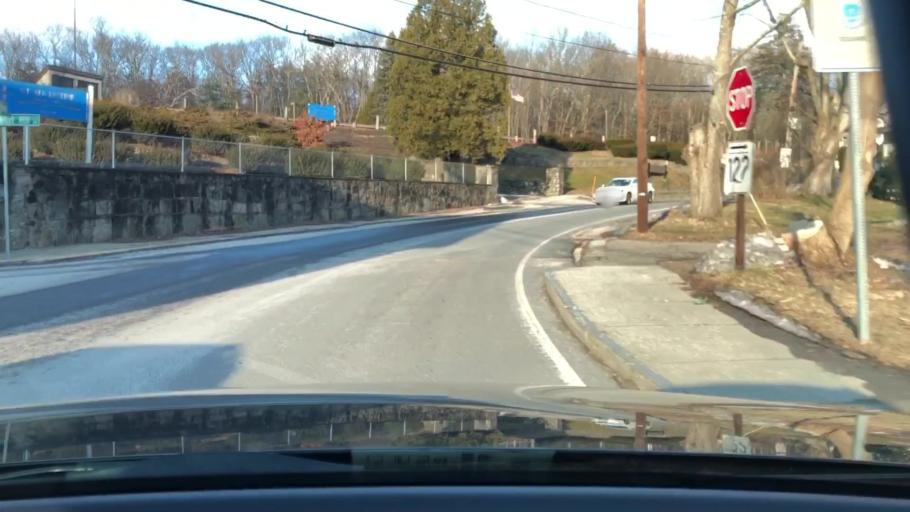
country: US
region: Massachusetts
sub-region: Worcester County
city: Millville
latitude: 42.0280
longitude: -71.5801
